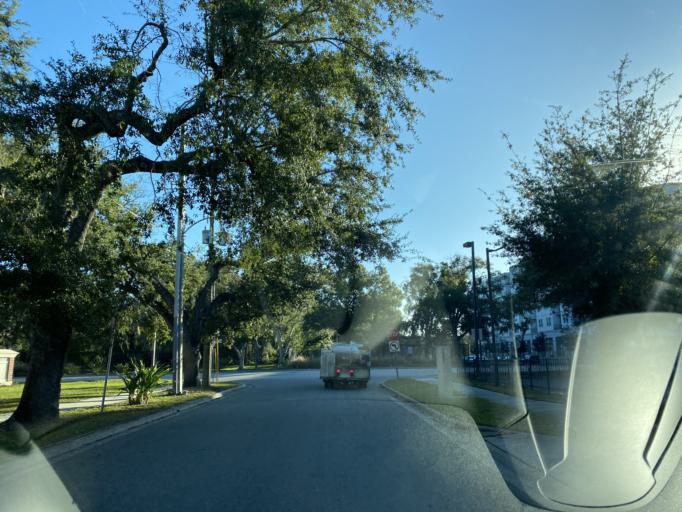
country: US
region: Florida
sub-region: Orange County
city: Orlando
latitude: 28.5511
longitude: -81.3896
